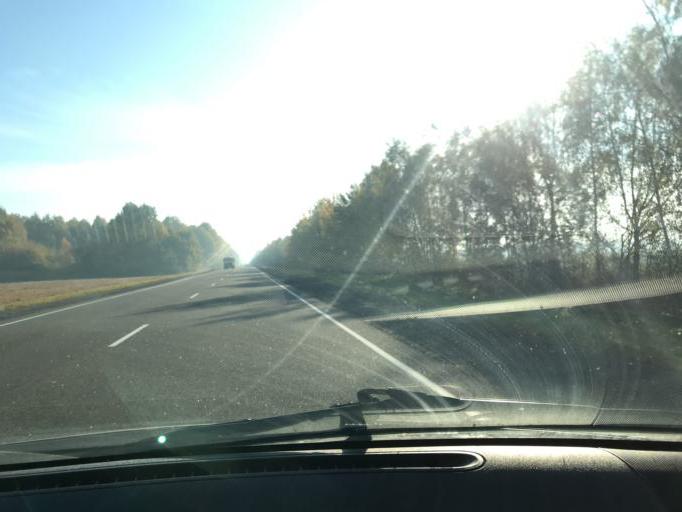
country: BY
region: Brest
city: Horad Luninyets
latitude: 52.3036
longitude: 26.7065
